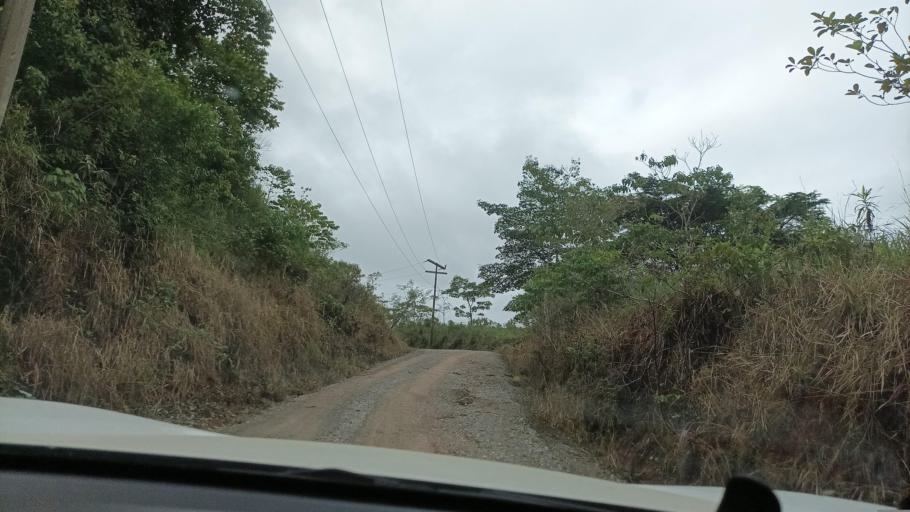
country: MX
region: Veracruz
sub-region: Uxpanapa
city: Poblado 10
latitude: 17.4241
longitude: -94.4184
